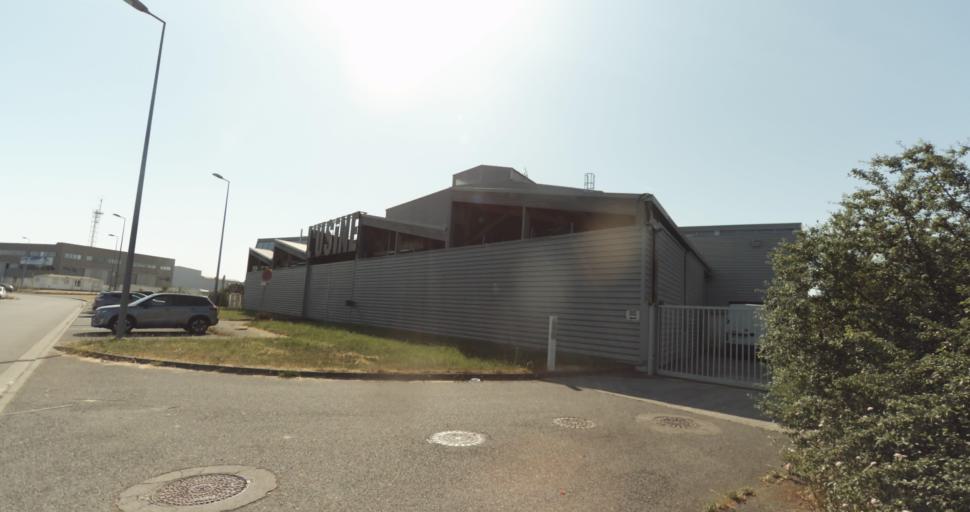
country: FR
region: Midi-Pyrenees
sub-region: Departement de la Haute-Garonne
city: Tournefeuille
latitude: 43.5907
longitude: 1.3074
